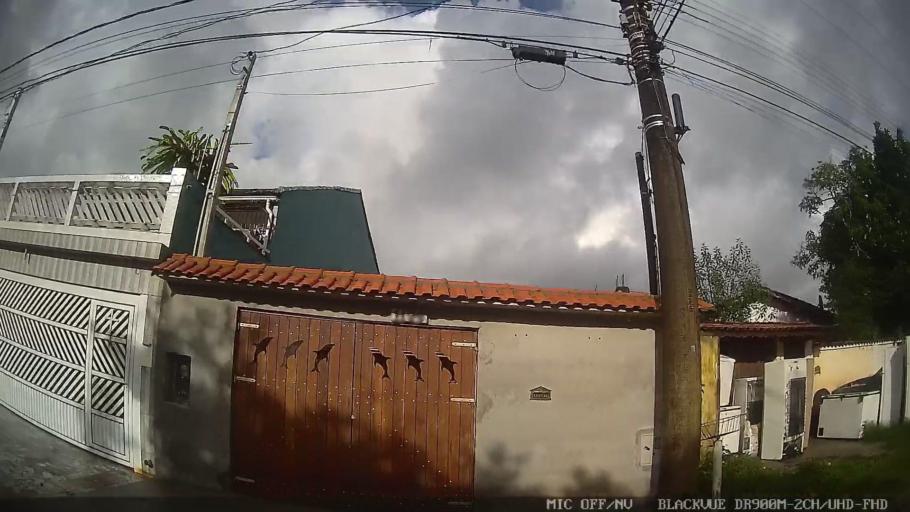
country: BR
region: Sao Paulo
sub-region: Itanhaem
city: Itanhaem
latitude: -24.2258
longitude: -46.8908
